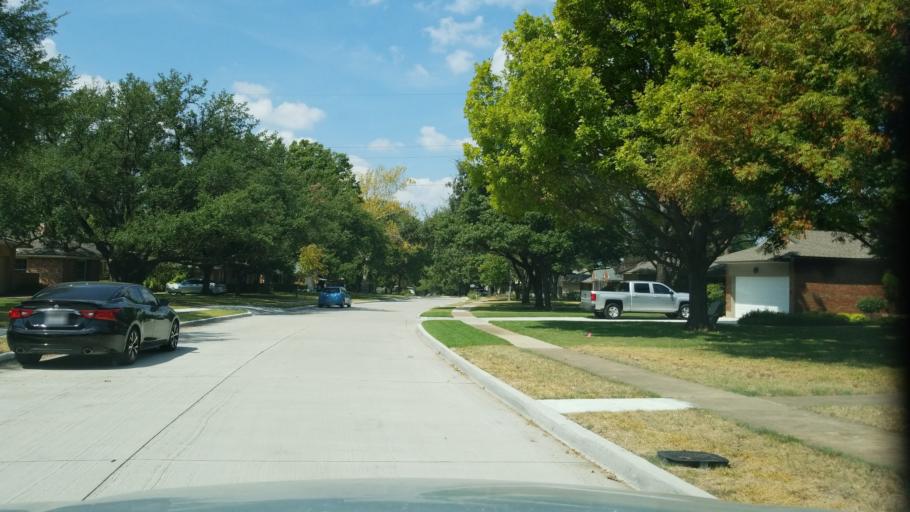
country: US
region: Texas
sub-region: Dallas County
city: Richardson
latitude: 32.9573
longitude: -96.7443
